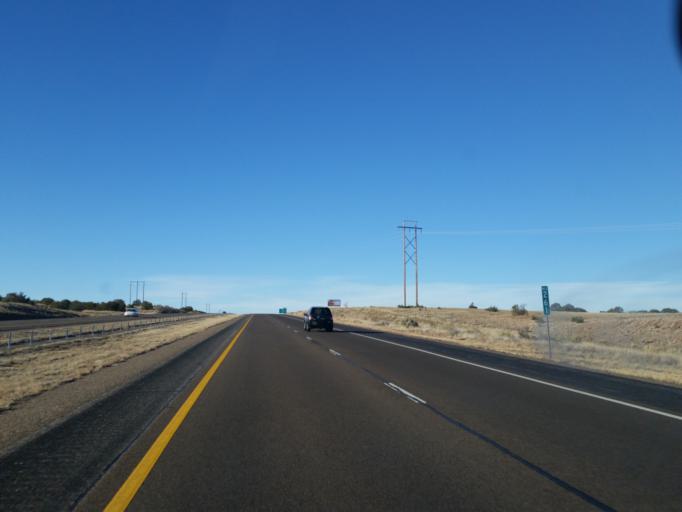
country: US
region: New Mexico
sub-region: Sandoval County
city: Santo Domingo Pueblo
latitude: 35.4814
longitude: -106.2778
